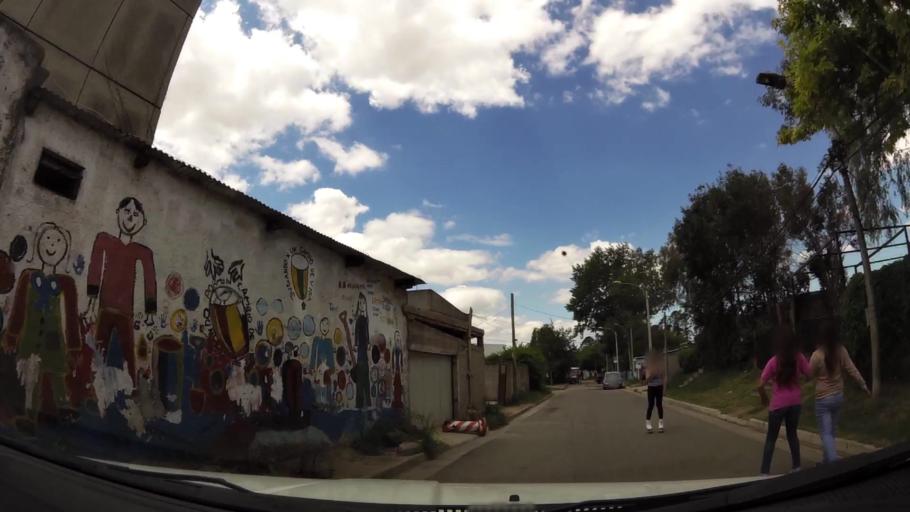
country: UY
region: Canelones
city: La Paz
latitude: -34.8206
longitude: -56.2486
